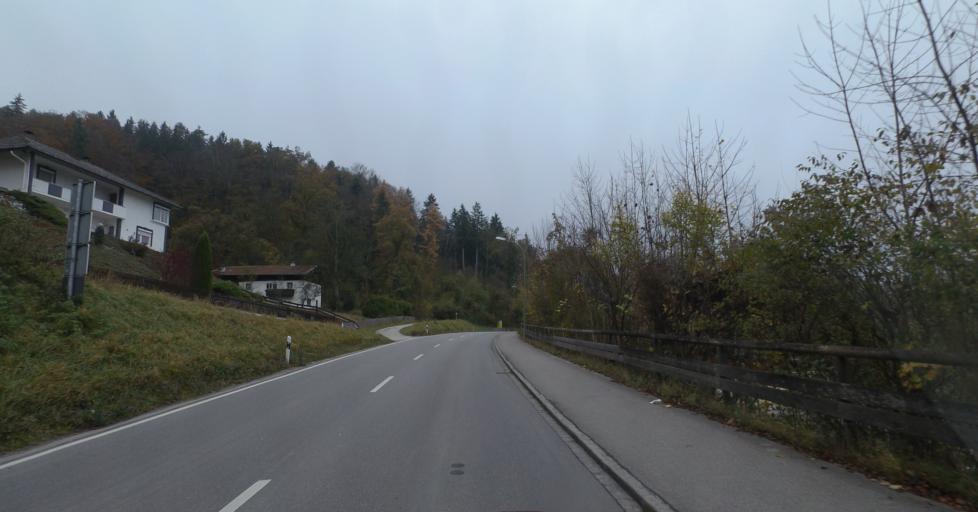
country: DE
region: Bavaria
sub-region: Upper Bavaria
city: Trostberg an der Alz
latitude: 48.0366
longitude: 12.5603
